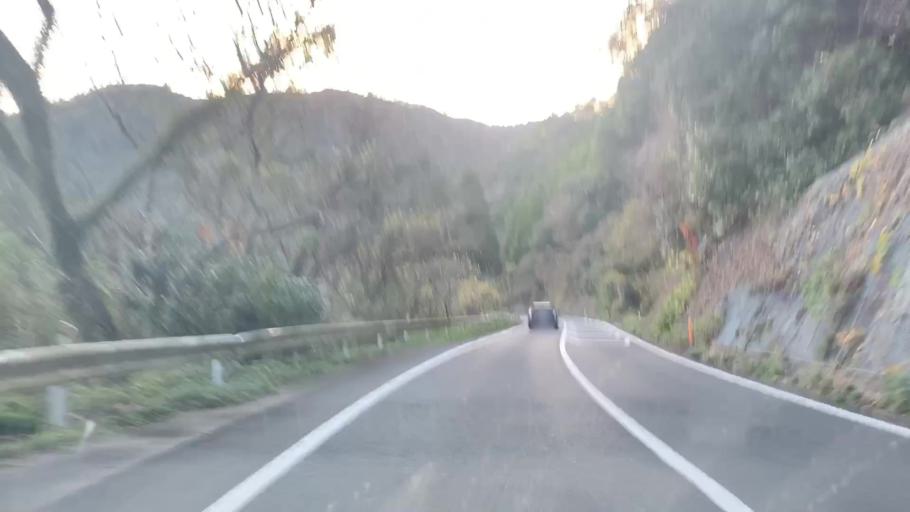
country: JP
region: Saga Prefecture
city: Karatsu
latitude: 33.3370
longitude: 129.9728
